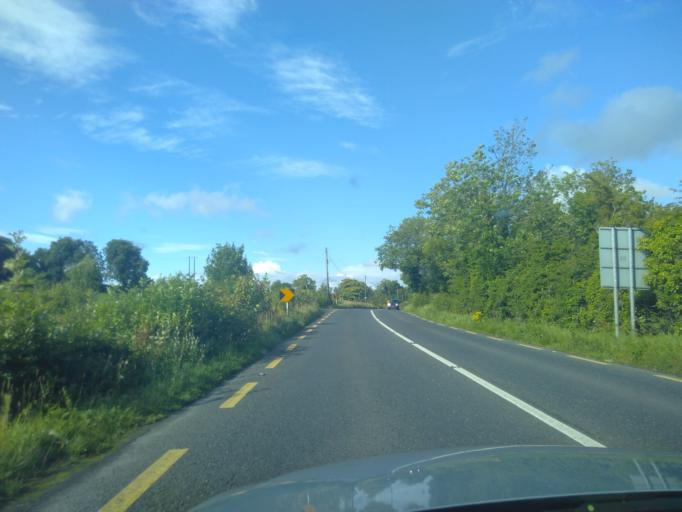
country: IE
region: Ulster
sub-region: County Donegal
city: Ballybofey
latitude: 54.8206
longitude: -7.7559
